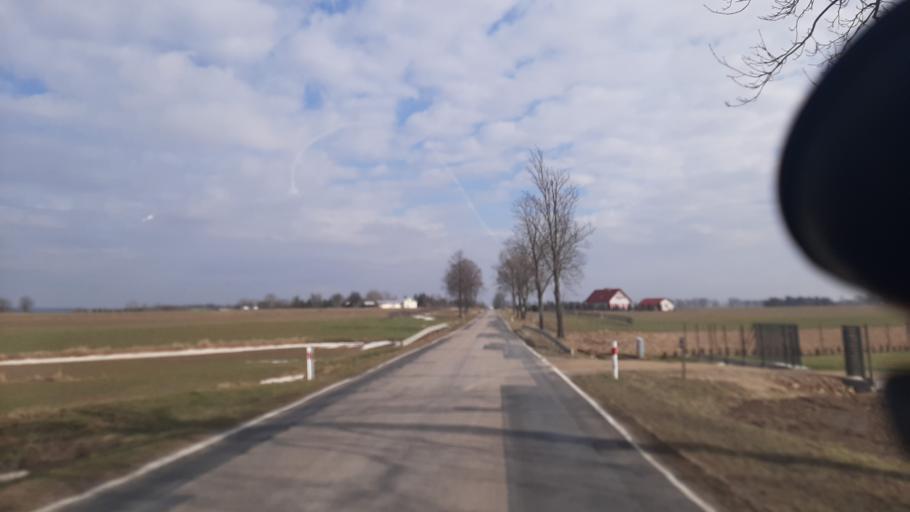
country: PL
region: Lublin Voivodeship
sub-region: Powiat lubelski
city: Niemce
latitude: 51.3602
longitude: 22.5392
